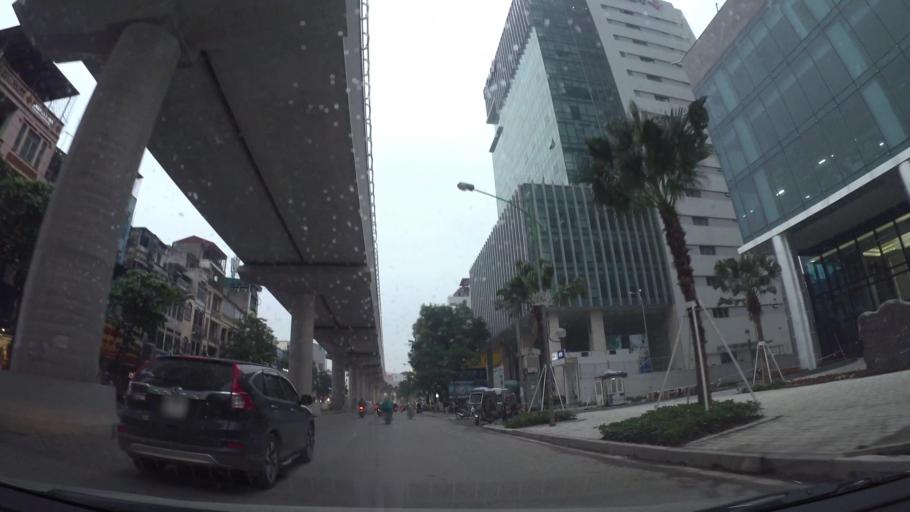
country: VN
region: Ha Noi
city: Cau Giay
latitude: 21.0348
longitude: 105.7949
